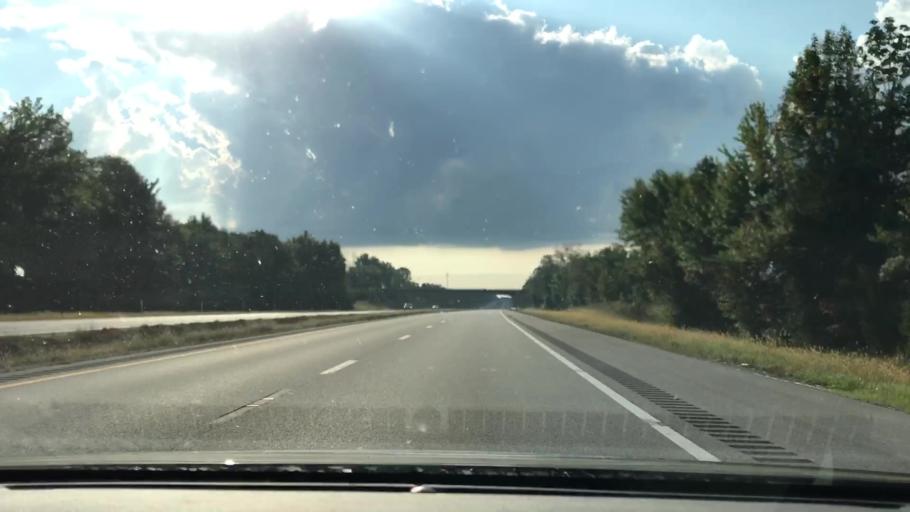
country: US
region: Kentucky
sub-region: Barren County
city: Cave City
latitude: 37.0395
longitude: -86.0628
